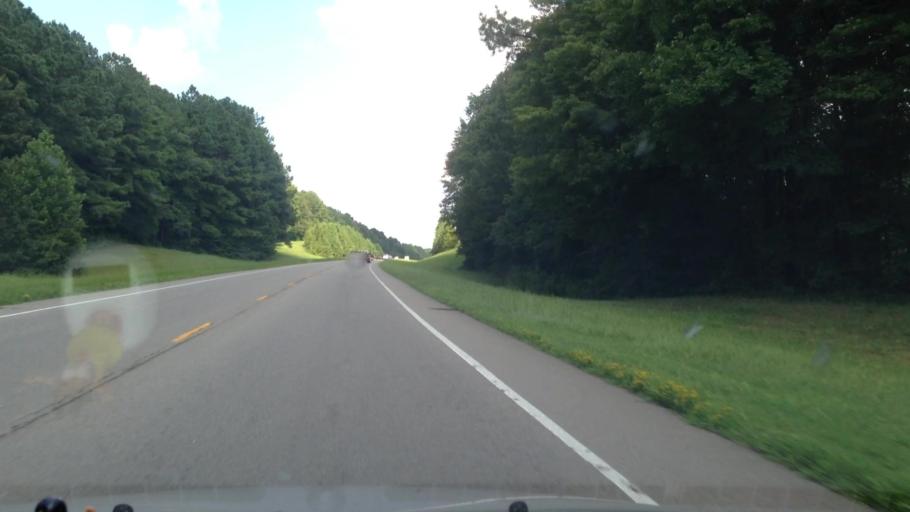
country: US
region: North Carolina
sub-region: Lee County
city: Broadway
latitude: 35.4396
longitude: -79.0760
